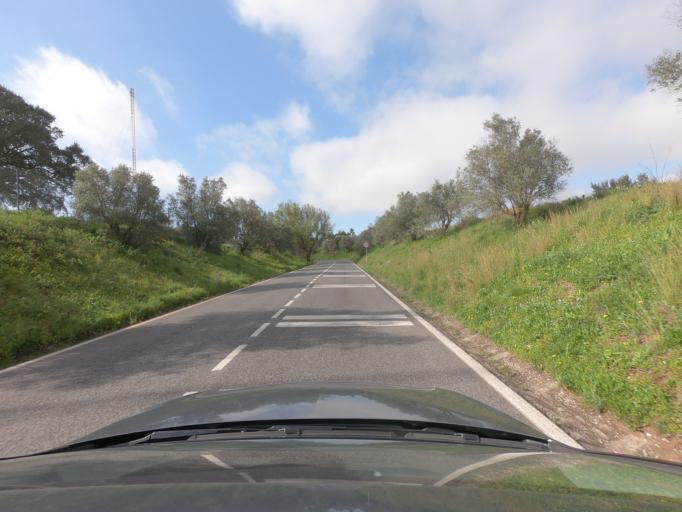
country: PT
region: Lisbon
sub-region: Oeiras
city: Quejas
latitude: 38.7256
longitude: -9.2710
